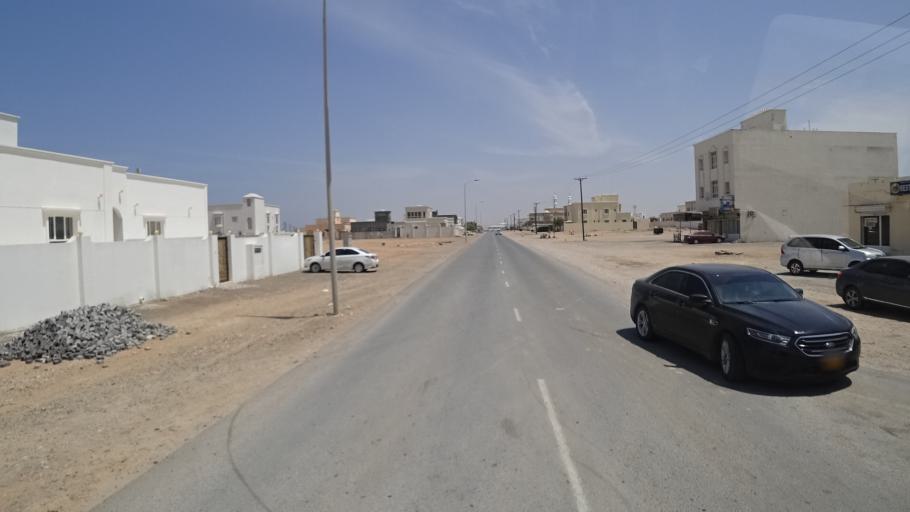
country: OM
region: Ash Sharqiyah
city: Sur
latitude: 22.6150
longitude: 59.4622
